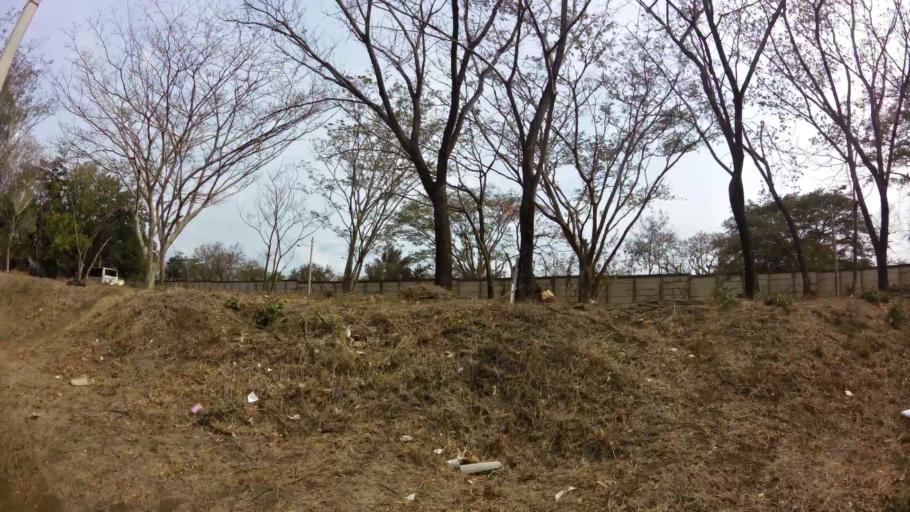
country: NI
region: Managua
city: Managua
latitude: 12.1486
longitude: -86.2486
